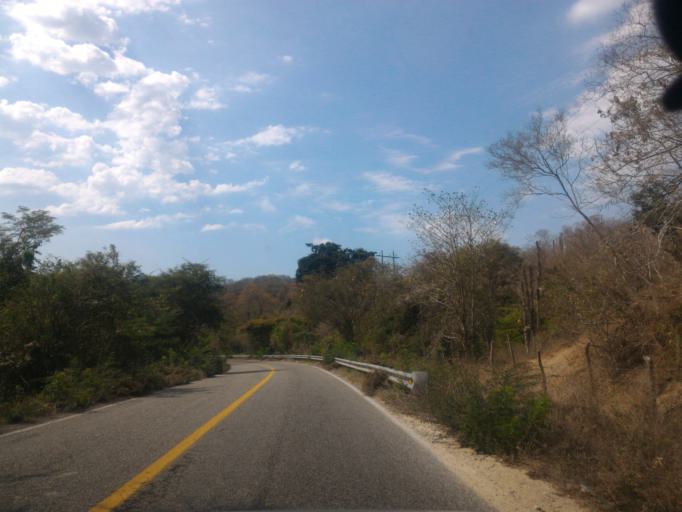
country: MX
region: Michoacan
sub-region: Coalcoman de Vazquez Pallares
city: Coalcoman de Vazquez Pallares
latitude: 18.2858
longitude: -103.3652
